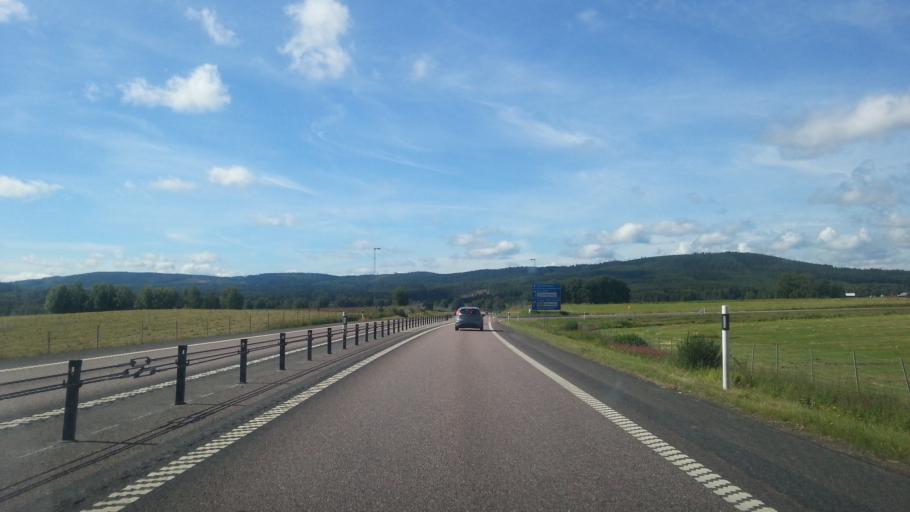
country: SE
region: Dalarna
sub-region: Borlange Kommun
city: Borlaenge
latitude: 60.4287
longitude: 15.3354
